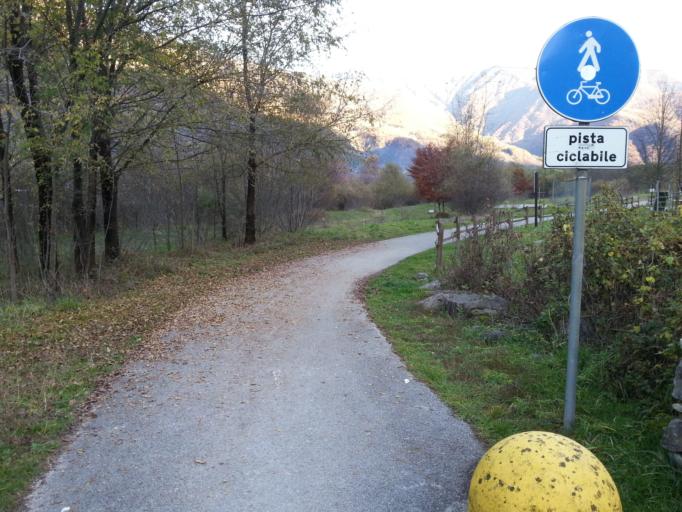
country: IT
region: Lombardy
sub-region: Provincia di Lecco
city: Primaluna
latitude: 45.9830
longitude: 9.4244
